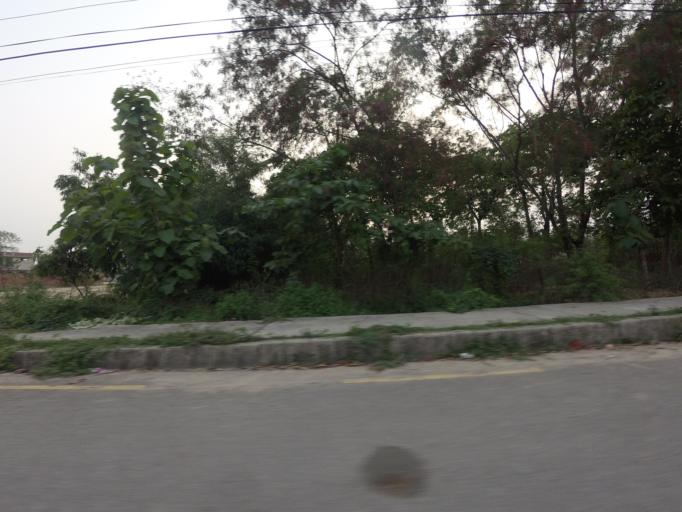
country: NP
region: Western Region
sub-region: Lumbini Zone
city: Bhairahawa
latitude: 27.5030
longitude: 83.4637
